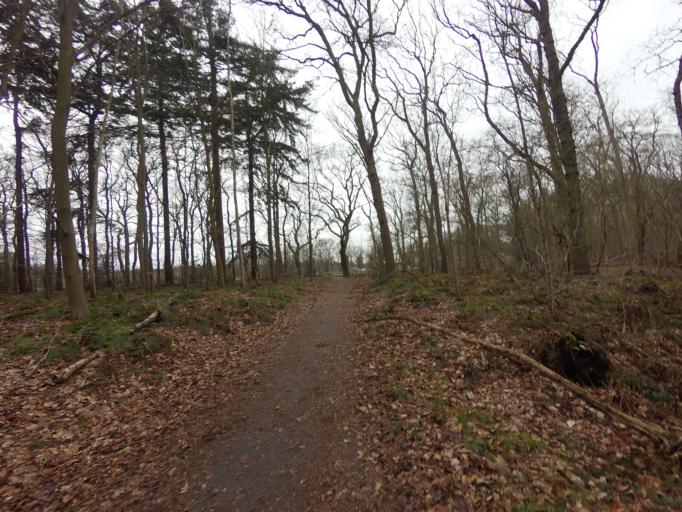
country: NL
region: Friesland
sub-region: Gemeente Gaasterlan-Sleat
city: Oudemirdum
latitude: 52.8640
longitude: 5.5405
